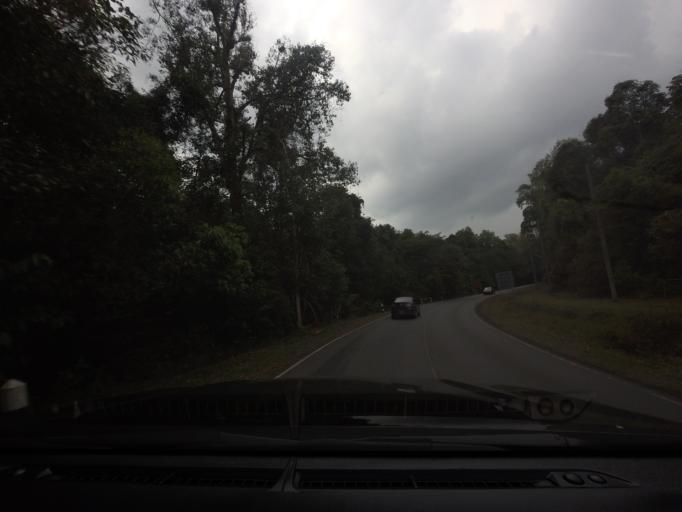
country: TH
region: Sara Buri
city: Muak Lek
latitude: 14.4381
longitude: 101.3700
